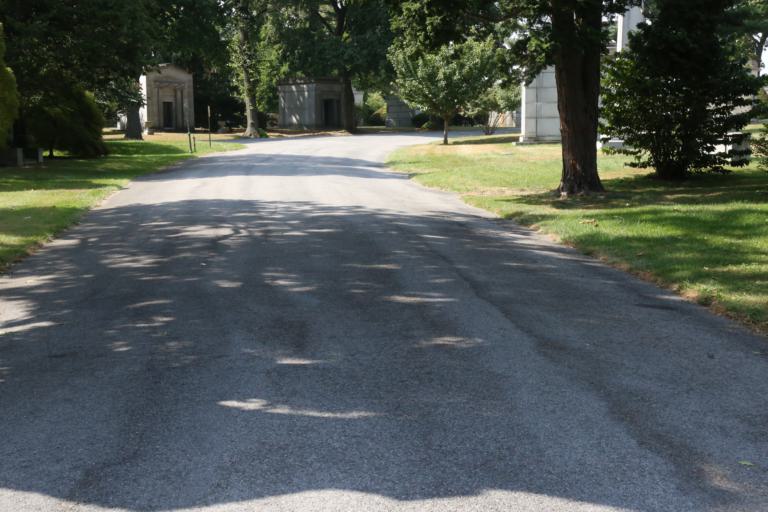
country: US
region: New York
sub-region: Westchester County
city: Yonkers
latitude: 40.8940
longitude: -73.8777
